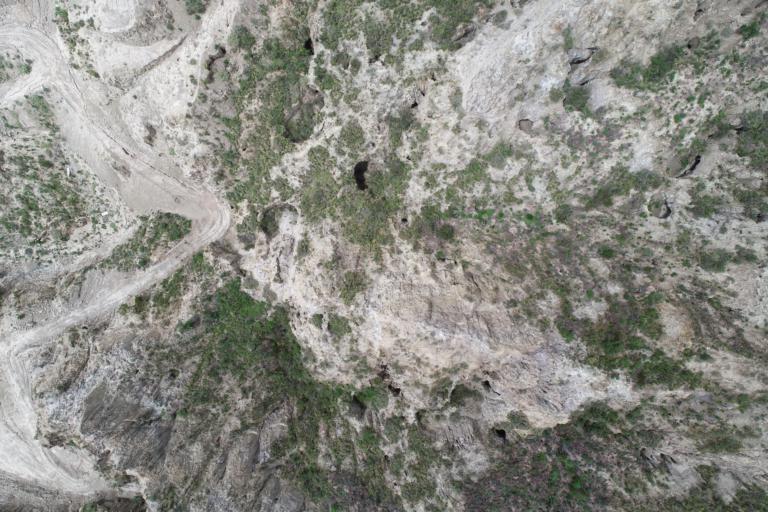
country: BO
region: La Paz
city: La Paz
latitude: -16.5437
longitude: -68.1184
